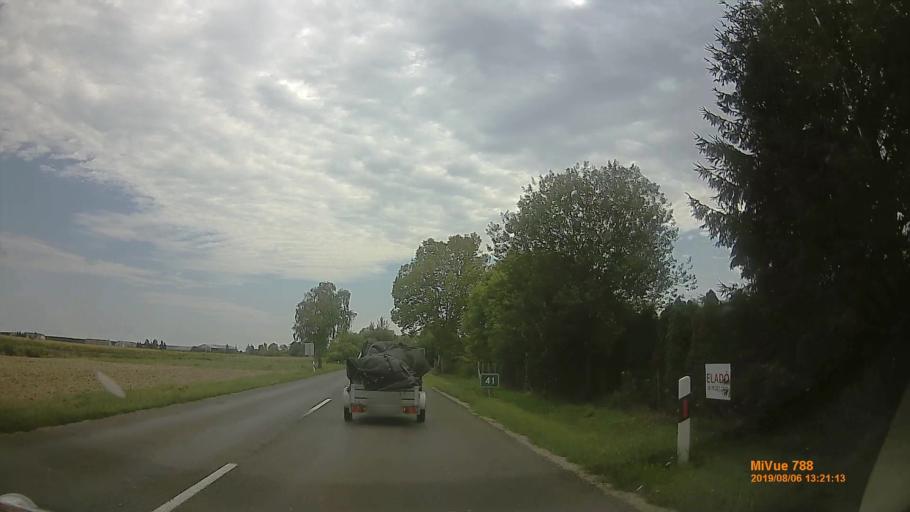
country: HU
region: Vas
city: Koszeg
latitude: 47.3454
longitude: 16.5755
